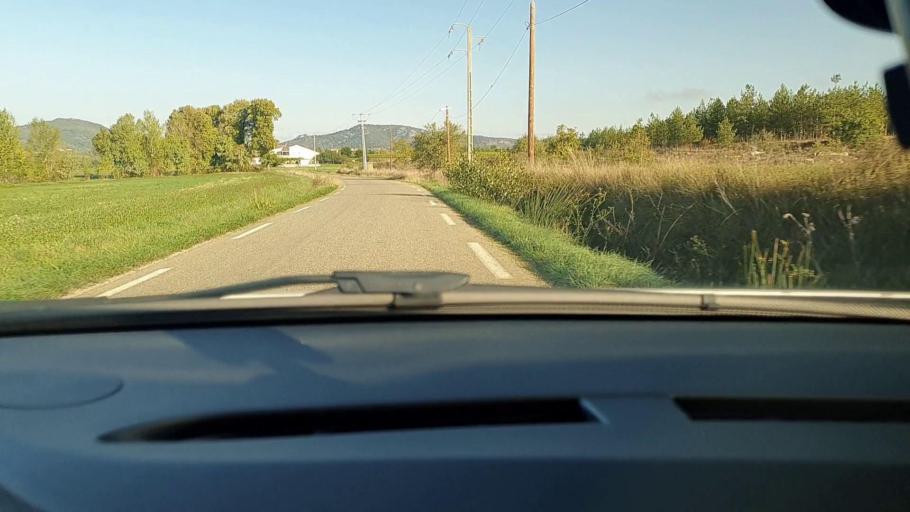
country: FR
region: Languedoc-Roussillon
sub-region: Departement du Gard
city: Saint-Ambroix
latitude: 44.2708
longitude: 4.2754
